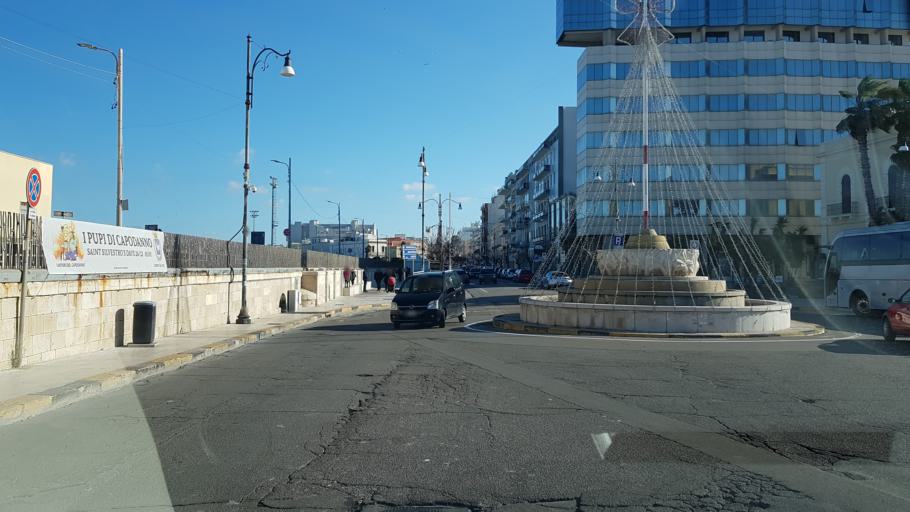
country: IT
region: Apulia
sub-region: Provincia di Lecce
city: Gallipoli
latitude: 40.0563
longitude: 17.9807
